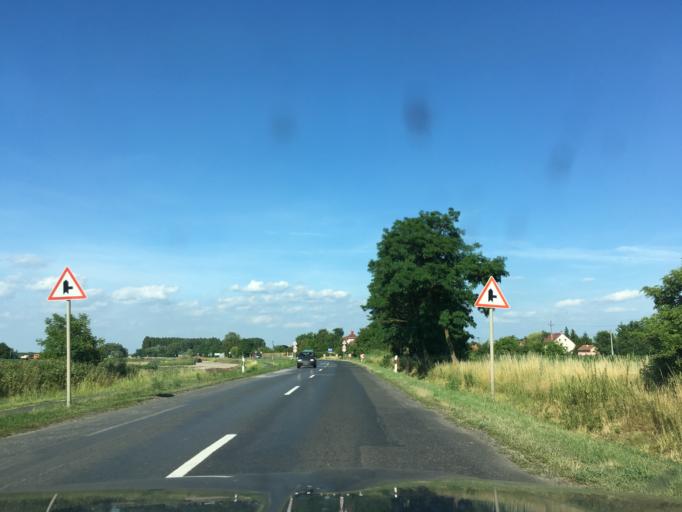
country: HU
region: Hajdu-Bihar
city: Hajdusamson
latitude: 47.5843
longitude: 21.7195
